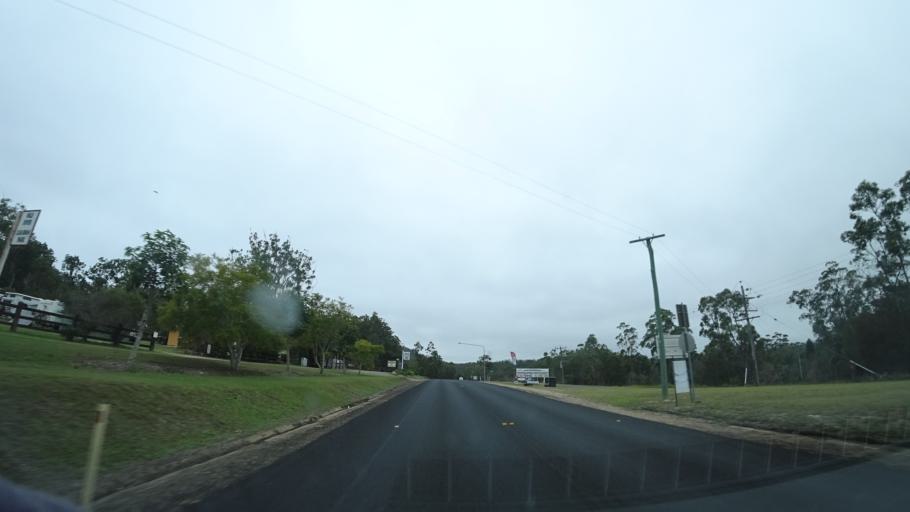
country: AU
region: Queensland
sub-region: Tablelands
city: Atherton
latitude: -17.3684
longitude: 145.3886
